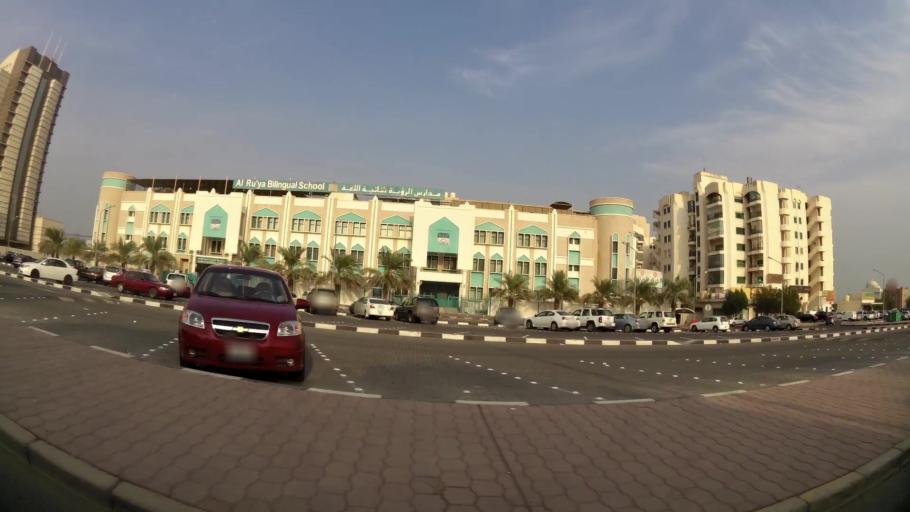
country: KW
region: Mubarak al Kabir
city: Sabah as Salim
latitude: 29.2479
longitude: 48.0813
